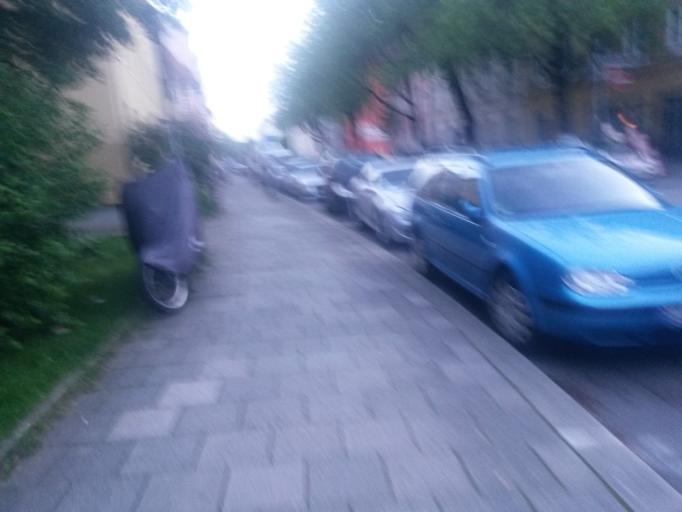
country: DE
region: Bavaria
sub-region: Upper Bavaria
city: Munich
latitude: 48.1282
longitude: 11.5851
